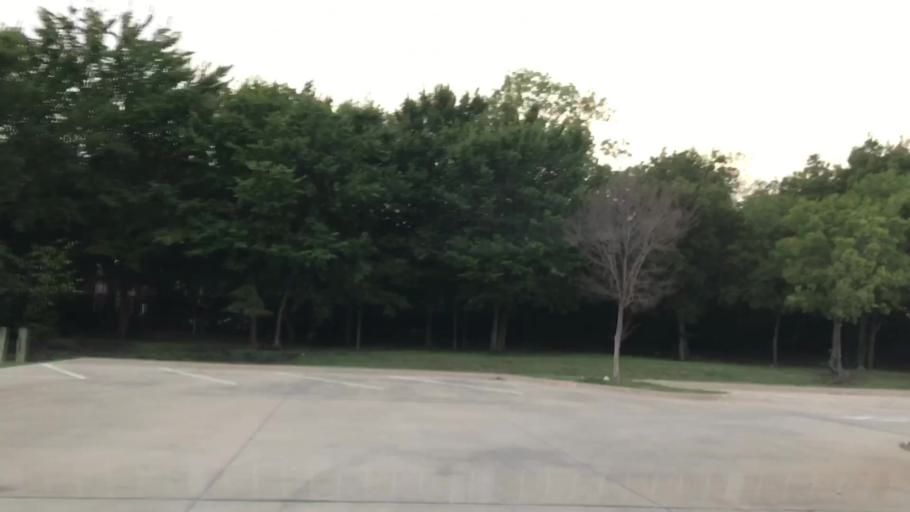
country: US
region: Texas
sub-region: Dallas County
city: Addison
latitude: 33.0100
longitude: -96.8201
